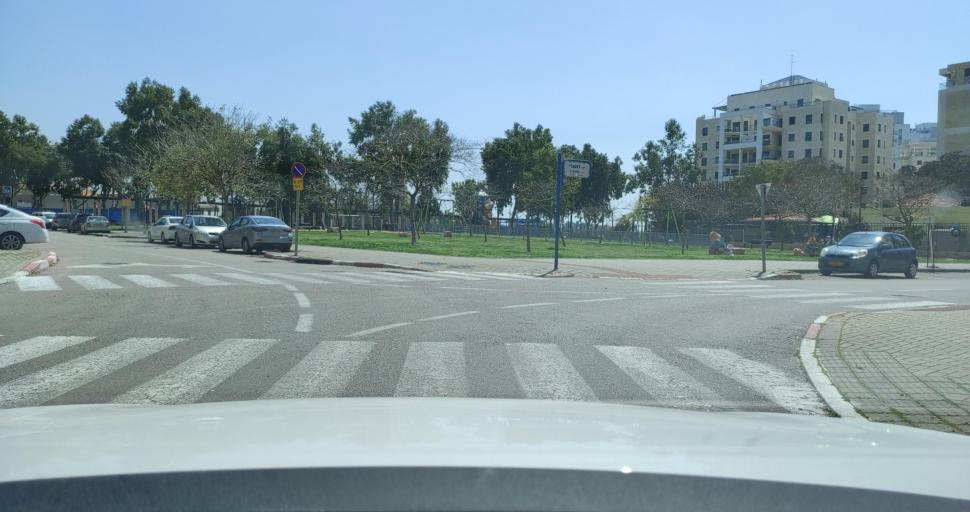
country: IL
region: Central District
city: Nordiyya
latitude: 32.2972
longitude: 34.8714
